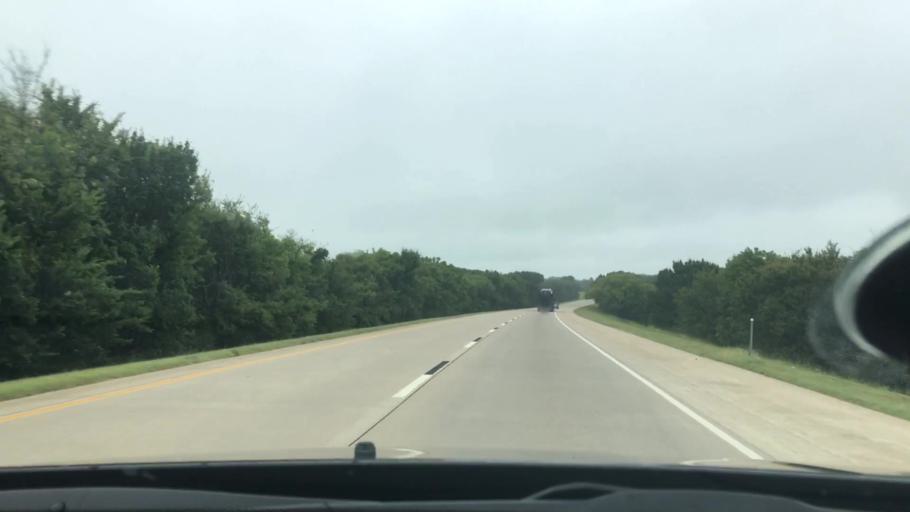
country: US
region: Oklahoma
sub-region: Okmulgee County
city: Henryetta
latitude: 35.4326
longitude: -95.9415
